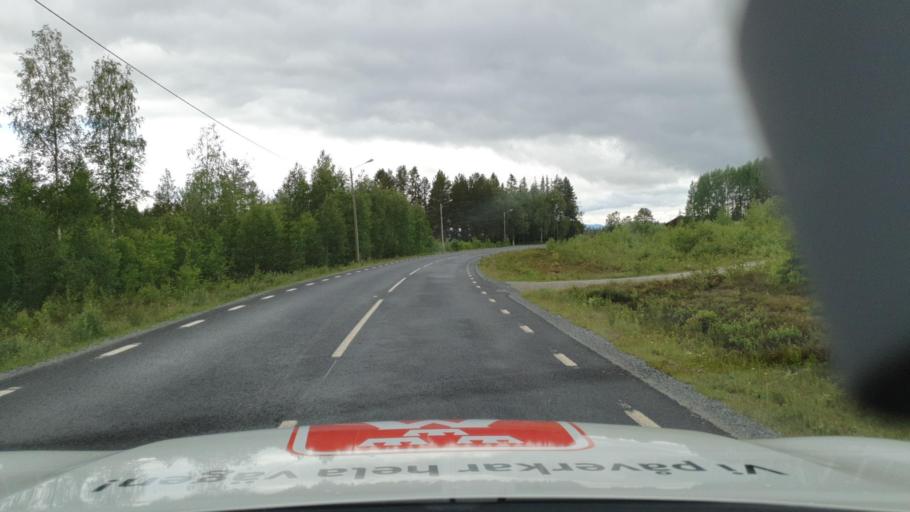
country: SE
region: Vaesterbotten
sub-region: Dorotea Kommun
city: Dorotea
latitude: 64.2178
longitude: 16.5461
